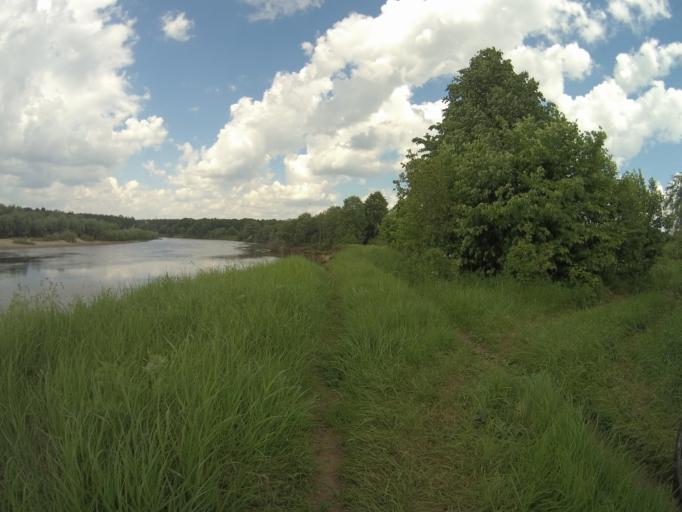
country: RU
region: Vladimir
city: Raduzhnyy
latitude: 56.0372
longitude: 40.2212
